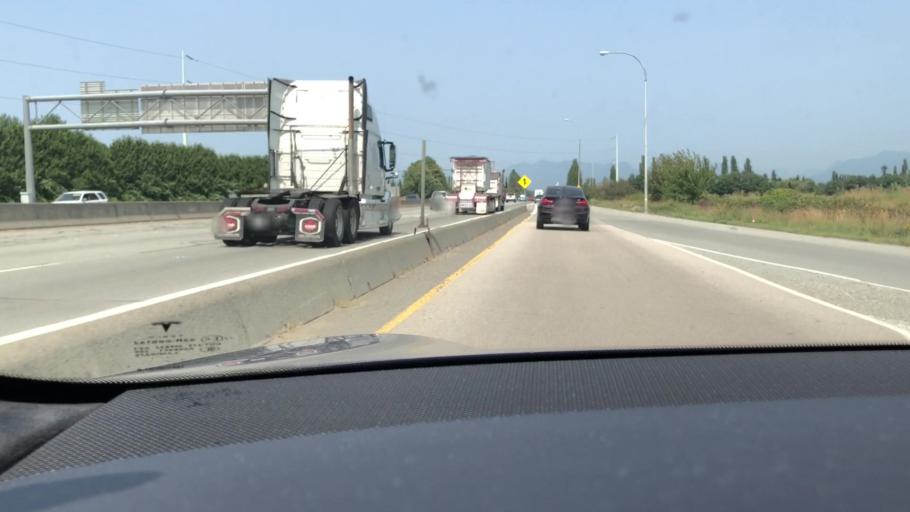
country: CA
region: British Columbia
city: Ladner
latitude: 49.1349
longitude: -123.0860
